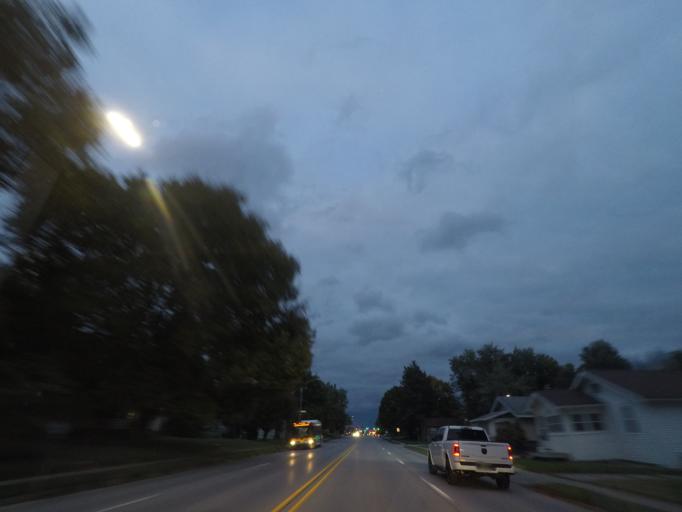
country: US
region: Iowa
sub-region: Story County
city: Ames
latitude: 42.0229
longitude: -93.6261
